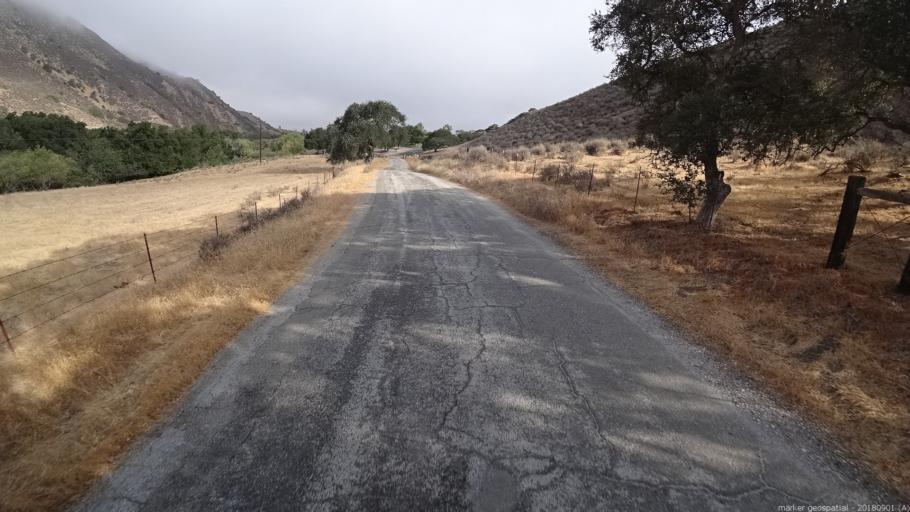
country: US
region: California
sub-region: Monterey County
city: Greenfield
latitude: 36.2632
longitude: -121.2956
